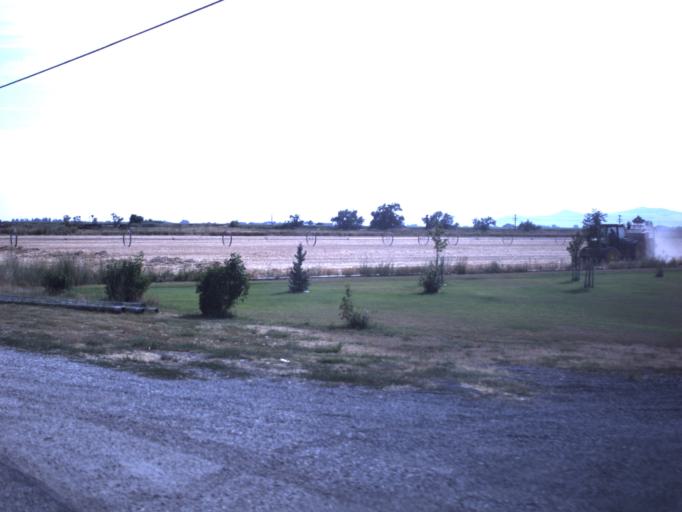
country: US
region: Utah
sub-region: Box Elder County
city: Honeyville
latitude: 41.6801
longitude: -112.0899
